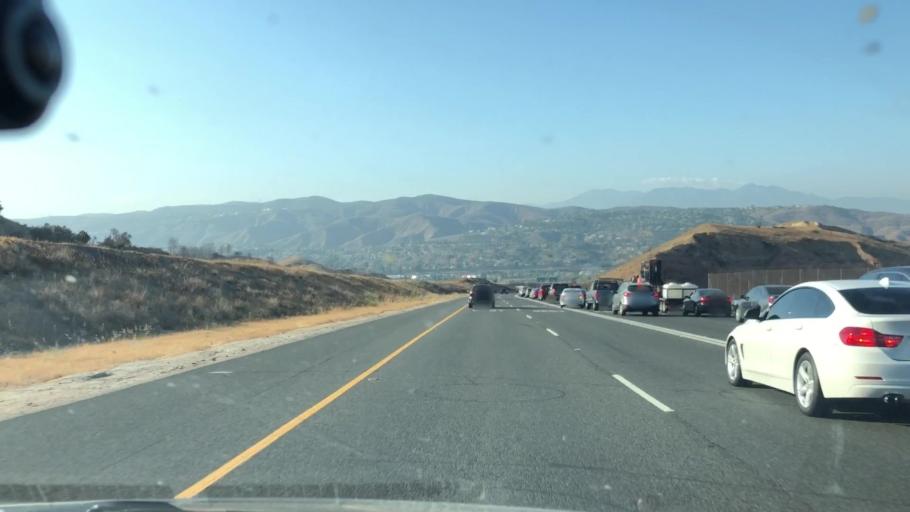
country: US
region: California
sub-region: Orange County
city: Yorba Linda
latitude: 33.8551
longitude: -117.7169
